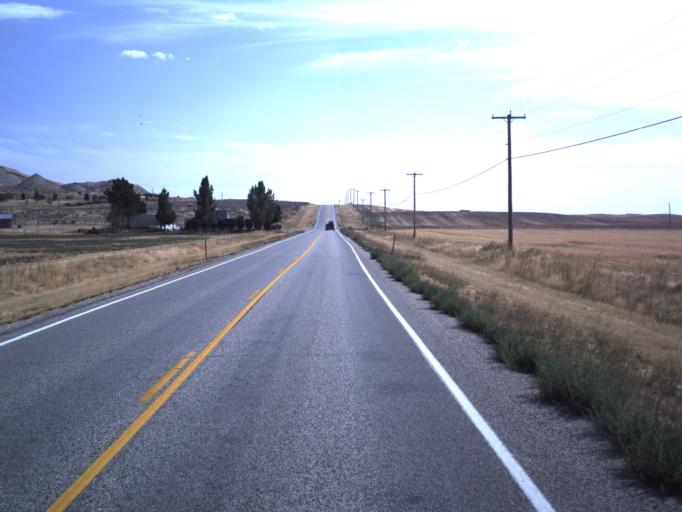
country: US
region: Utah
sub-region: Box Elder County
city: Garland
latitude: 41.7556
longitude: -112.0984
